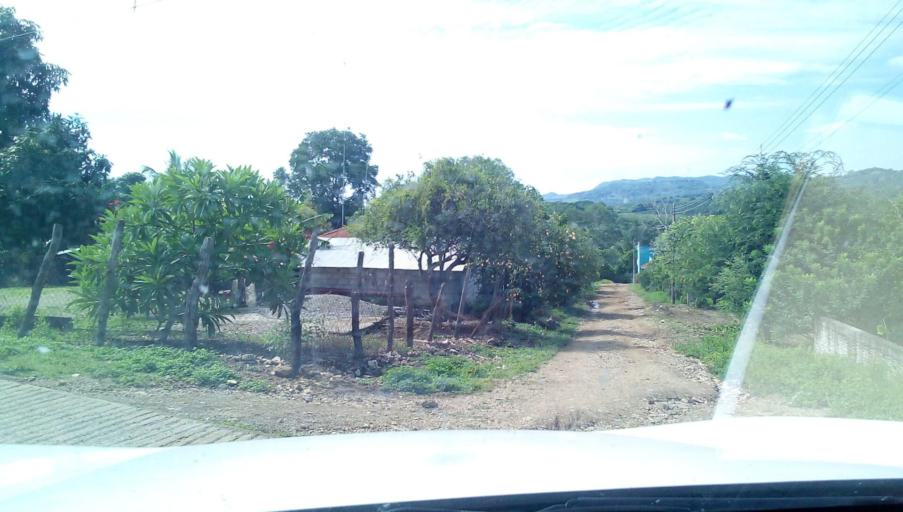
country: MX
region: Veracruz
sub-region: Alamo Temapache
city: Vegas de la Soledad y Soledad Dos
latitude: 20.8977
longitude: -97.9480
